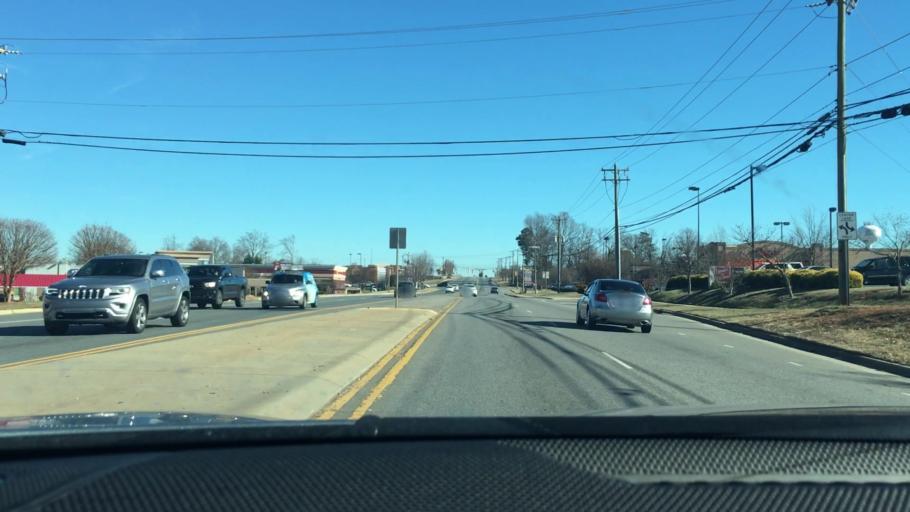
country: US
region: North Carolina
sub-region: Iredell County
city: Mooresville
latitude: 35.5959
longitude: -80.8756
